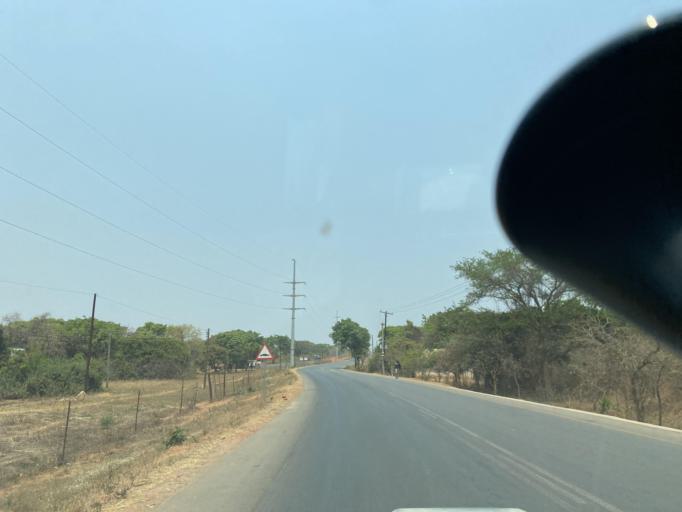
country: ZM
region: Lusaka
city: Lusaka
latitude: -15.5275
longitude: 28.4636
